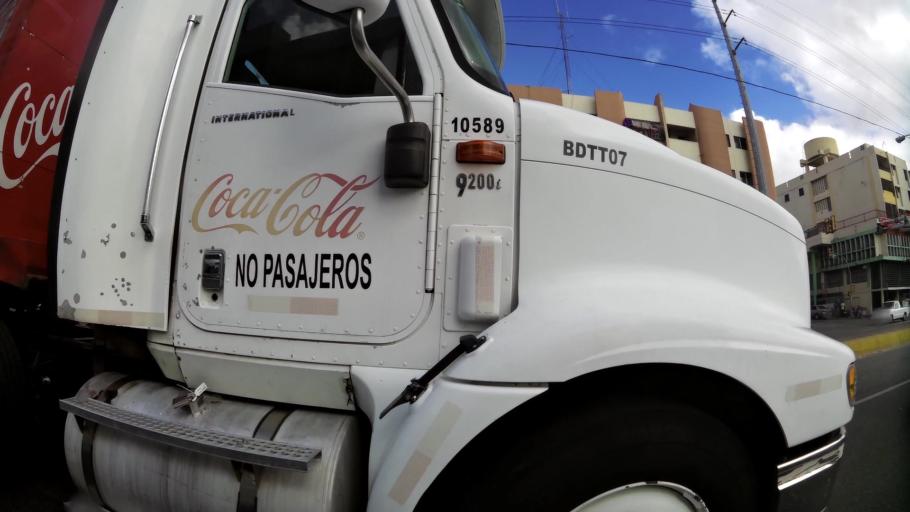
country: DO
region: Nacional
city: San Carlos
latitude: 18.4774
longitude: -69.8917
